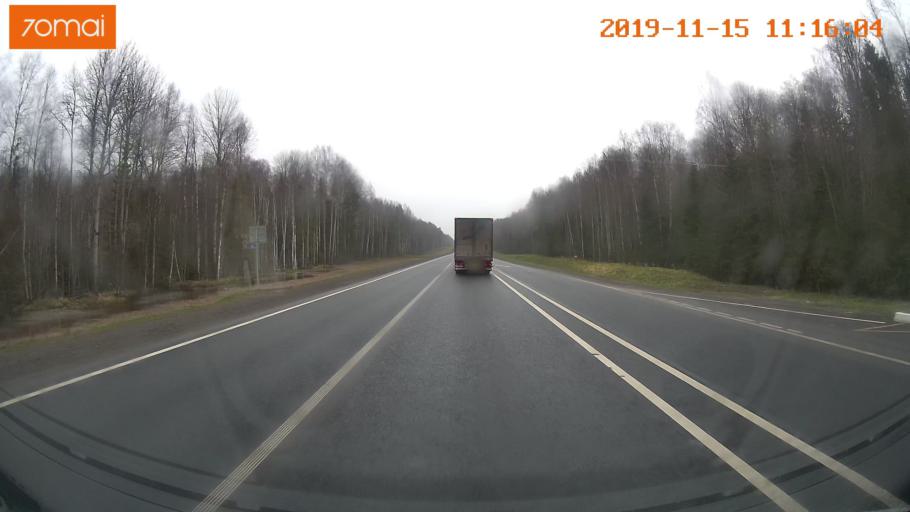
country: RU
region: Vologda
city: Chebsara
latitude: 59.1292
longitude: 39.2218
